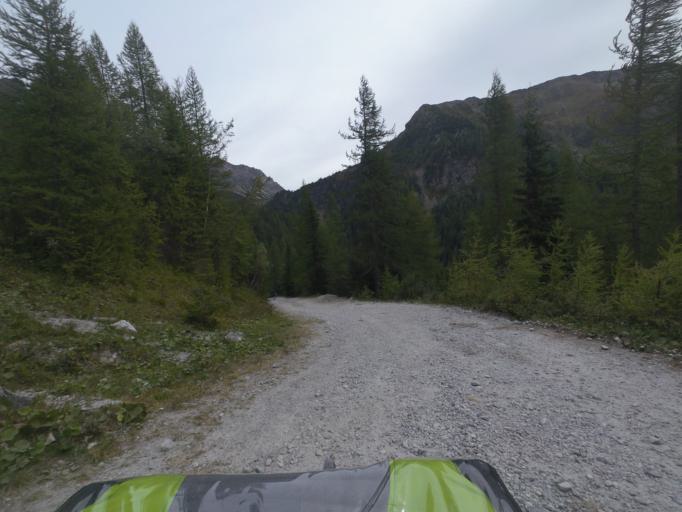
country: AT
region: Salzburg
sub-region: Politischer Bezirk Sankt Johann im Pongau
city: Untertauern
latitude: 47.2927
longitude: 13.5852
